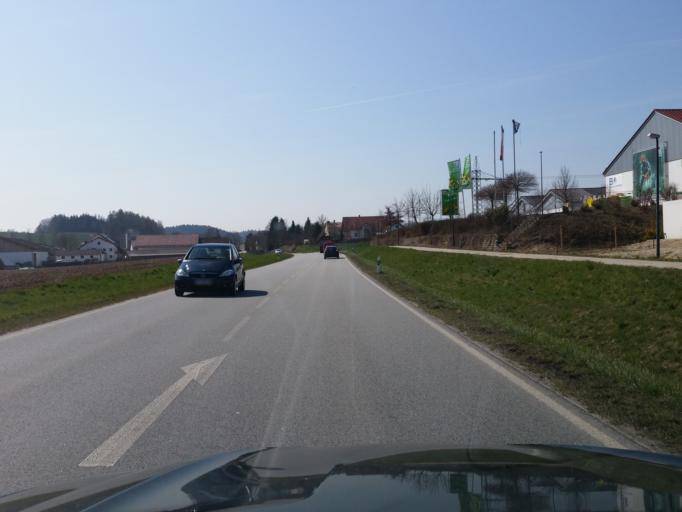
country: DE
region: Bavaria
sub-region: Lower Bavaria
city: Kumhausen
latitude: 48.5000
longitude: 12.1609
